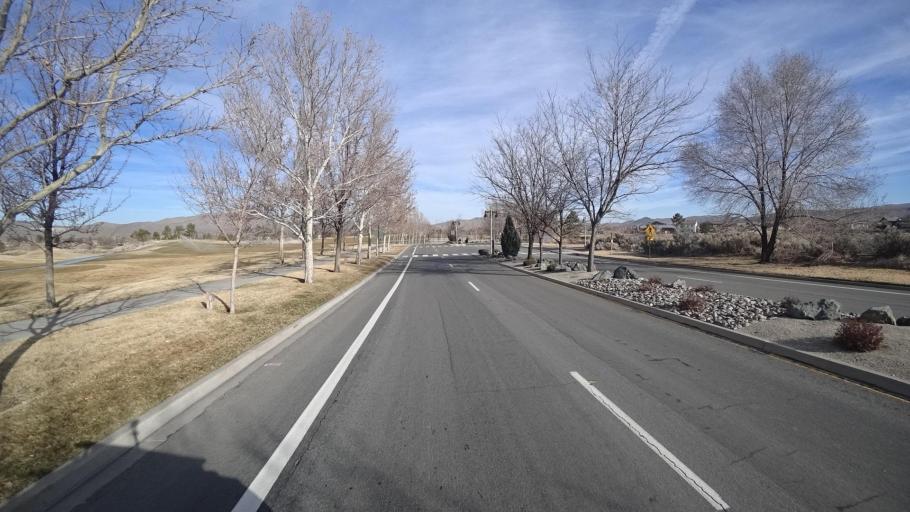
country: US
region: Nevada
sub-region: Washoe County
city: Spanish Springs
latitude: 39.6080
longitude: -119.6865
